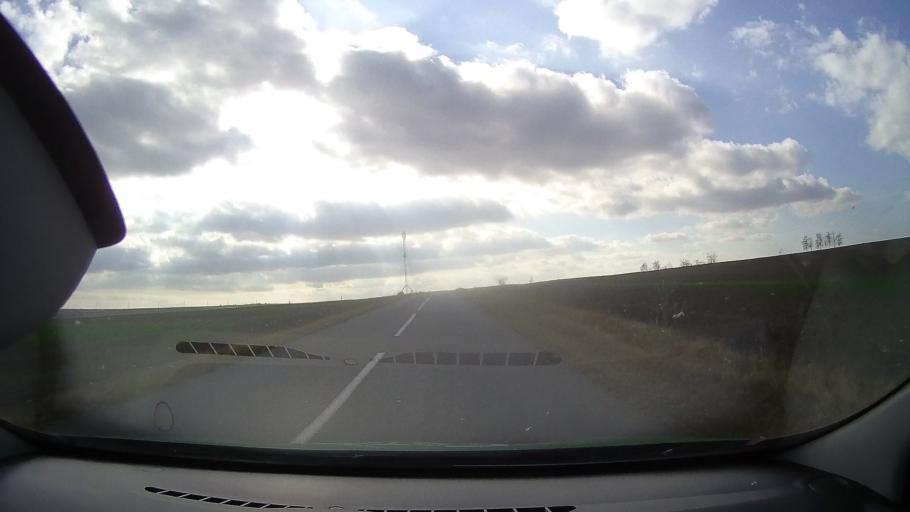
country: RO
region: Constanta
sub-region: Comuna Sacele
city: Sacele
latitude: 44.4939
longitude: 28.6558
